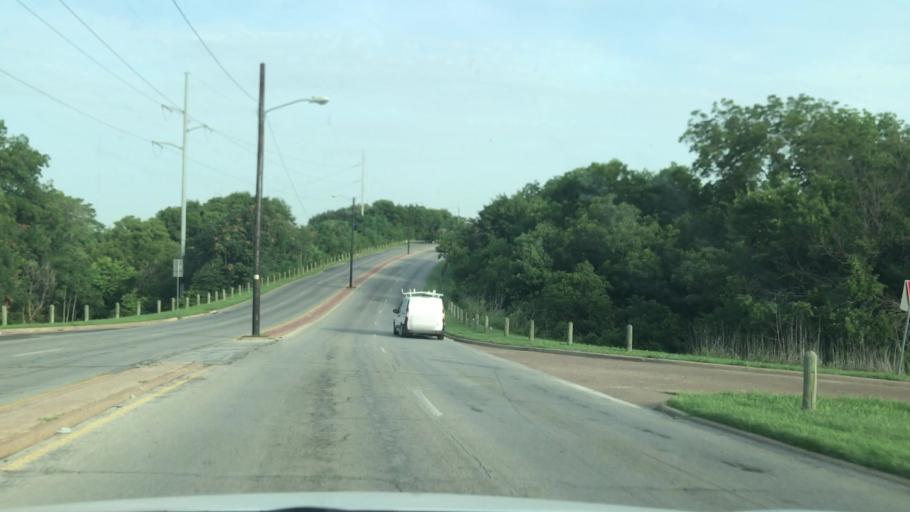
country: US
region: Texas
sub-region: Dallas County
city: Dallas
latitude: 32.7773
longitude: -96.7183
